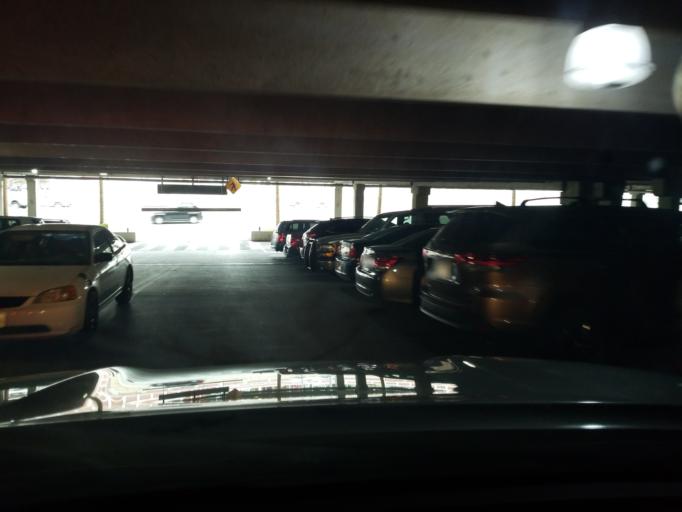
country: US
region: Texas
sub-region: Bexar County
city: Castle Hills
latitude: 29.5191
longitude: -98.4931
